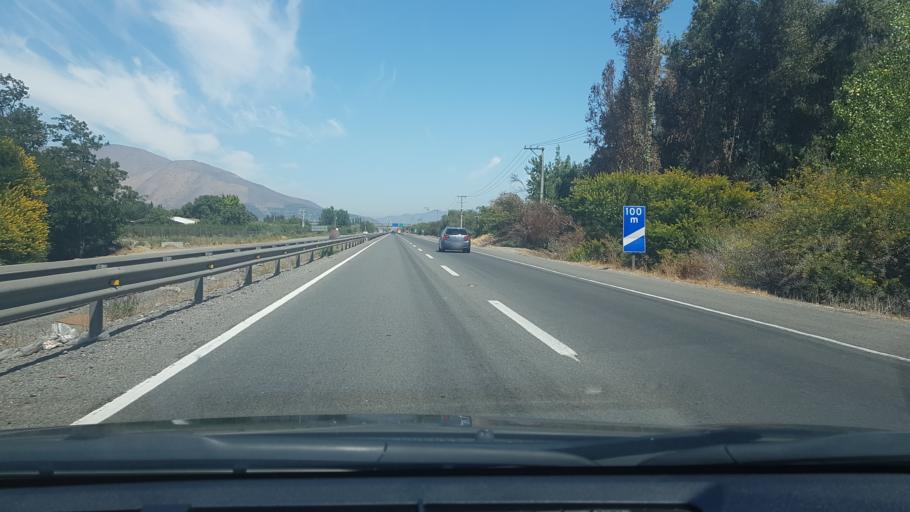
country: CL
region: Valparaiso
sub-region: Provincia de San Felipe
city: Llaillay
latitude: -32.8522
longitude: -70.9351
